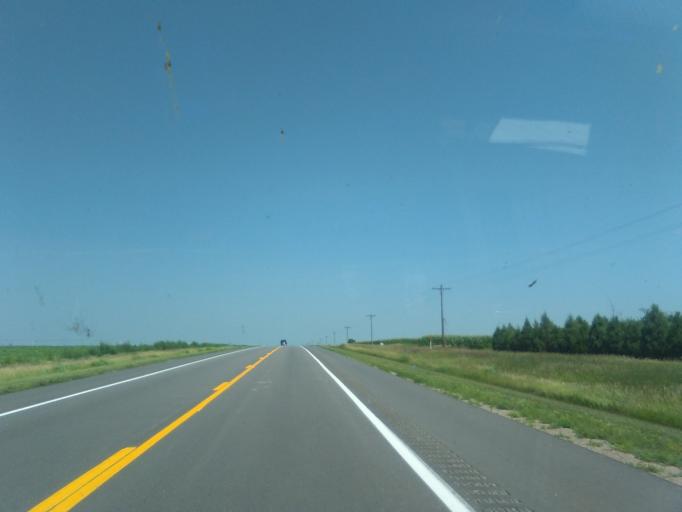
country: US
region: Nebraska
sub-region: Red Willow County
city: McCook
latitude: 40.3043
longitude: -100.6494
